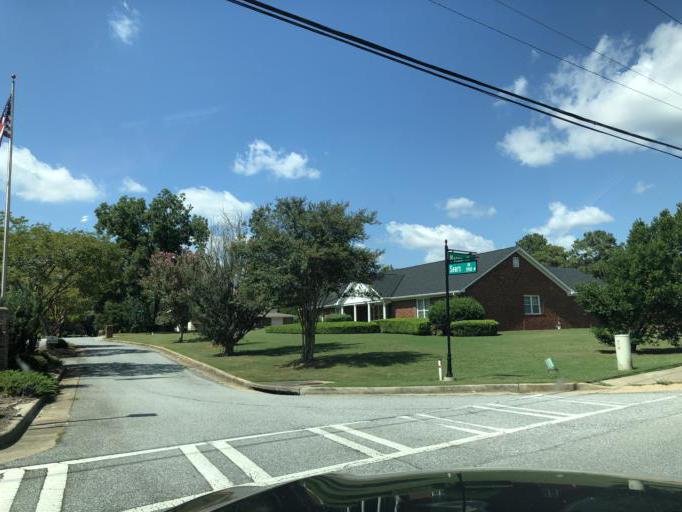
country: US
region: Georgia
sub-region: Muscogee County
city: Columbus
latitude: 32.4998
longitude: -84.9044
